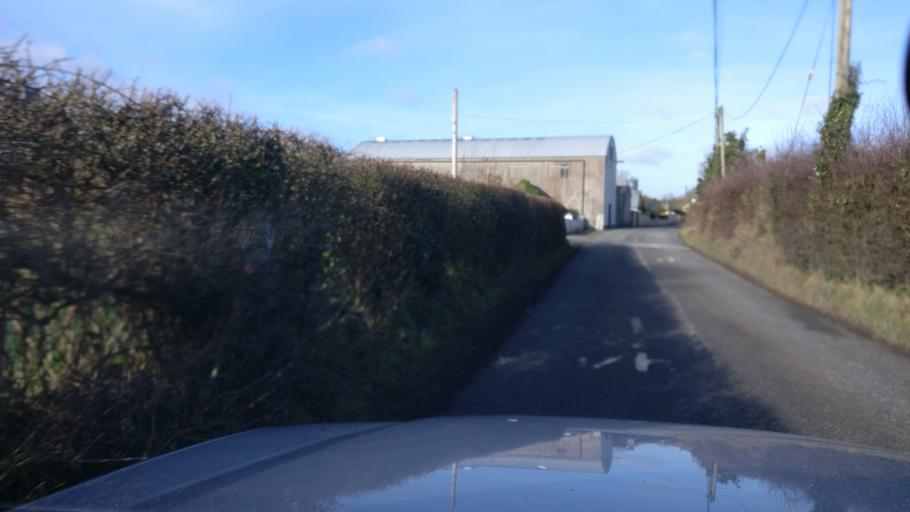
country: IE
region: Leinster
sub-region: Kilkenny
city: Castlecomer
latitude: 52.8633
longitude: -7.1646
